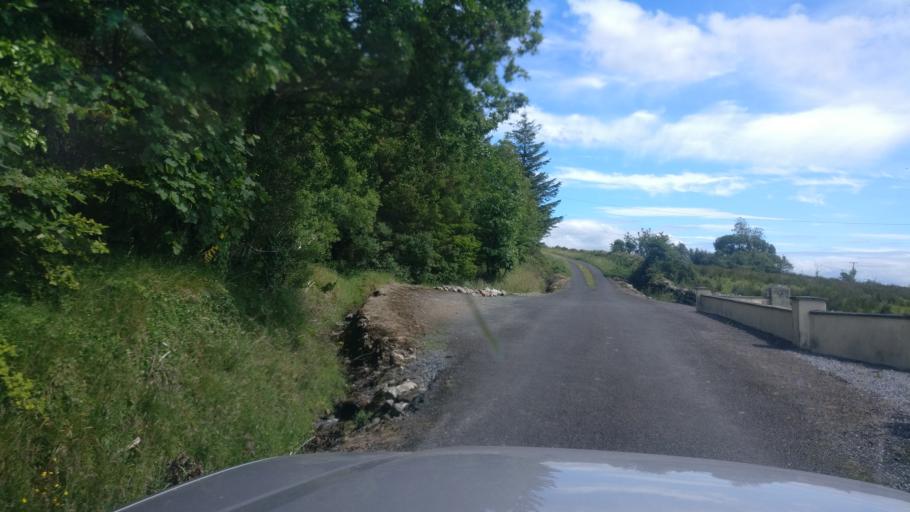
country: IE
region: Connaught
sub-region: County Galway
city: Gort
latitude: 53.0732
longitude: -8.7075
